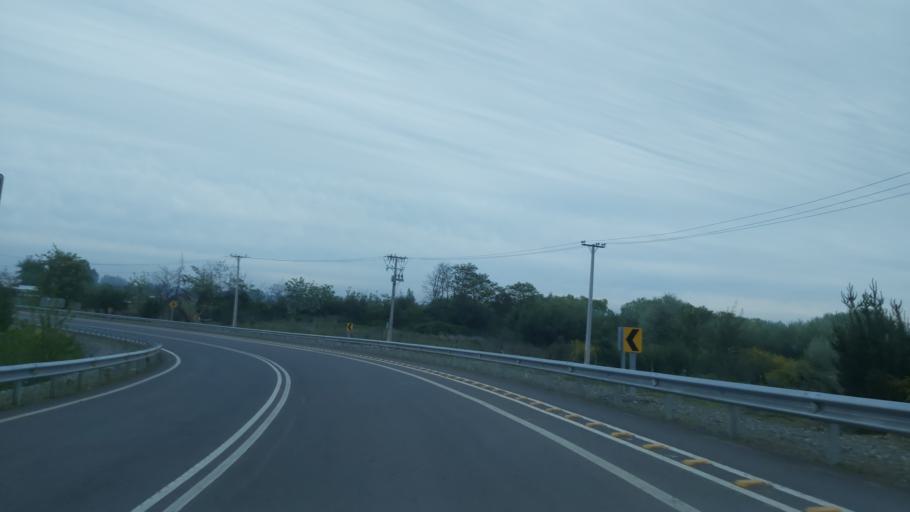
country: CL
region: Maule
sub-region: Provincia de Linares
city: Colbun
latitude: -35.6975
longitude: -71.4884
